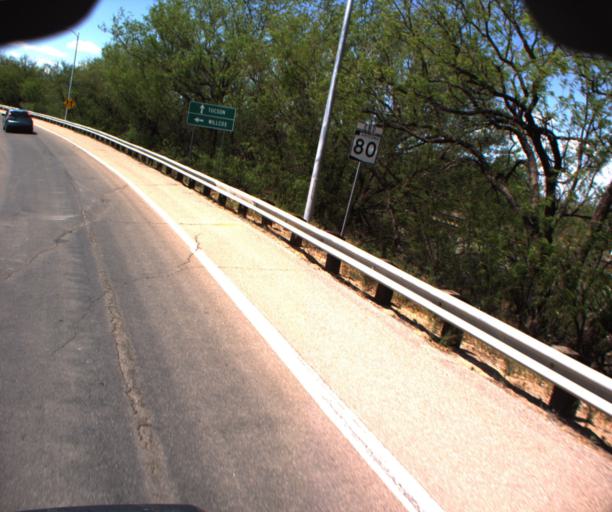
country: US
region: Arizona
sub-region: Cochise County
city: Benson
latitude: 31.9669
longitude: -110.2911
